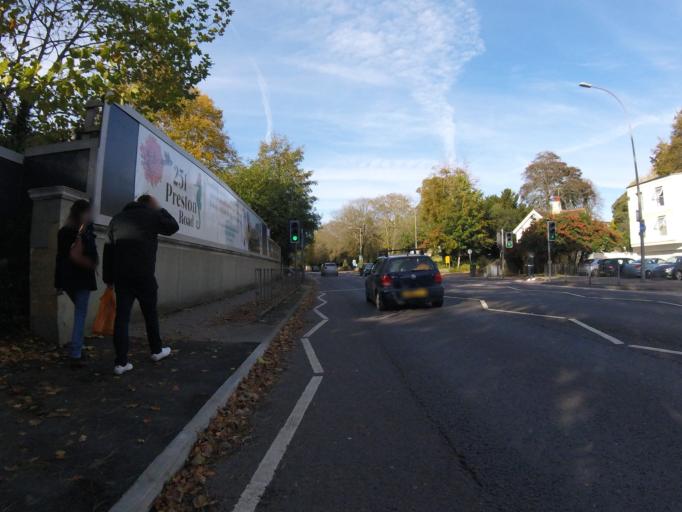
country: GB
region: England
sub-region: Brighton and Hove
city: Brighton
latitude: 50.8454
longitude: -0.1515
